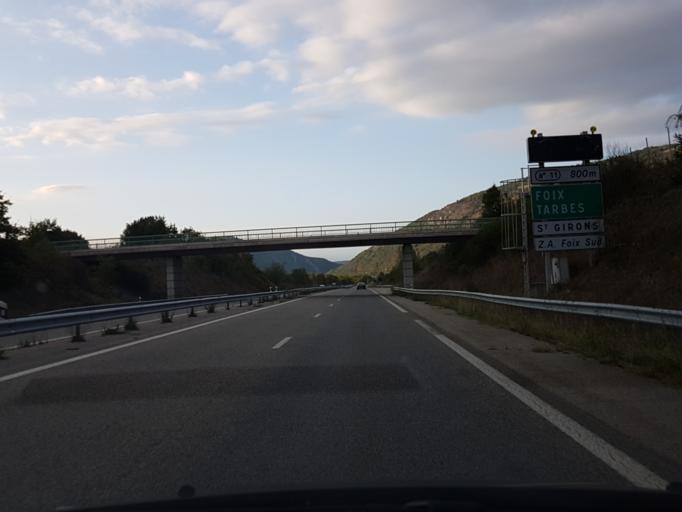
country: FR
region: Midi-Pyrenees
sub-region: Departement de l'Ariege
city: Montgaillard
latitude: 42.9377
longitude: 1.6253
